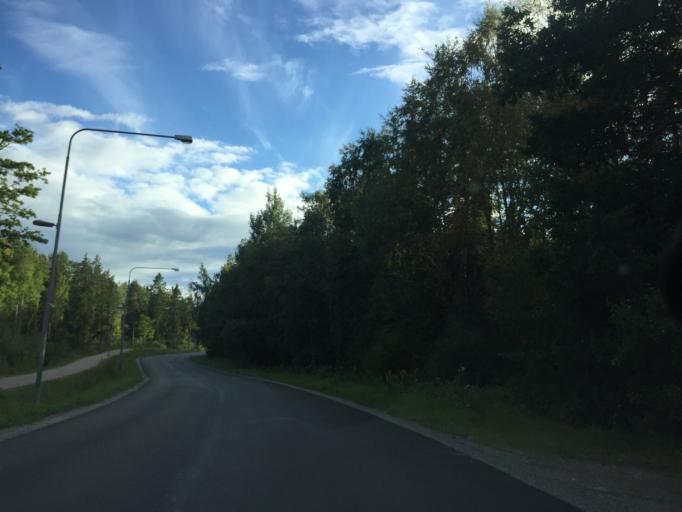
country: SE
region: Soedermanland
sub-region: Eskilstuna Kommun
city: Eskilstuna
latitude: 59.3535
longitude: 16.5128
